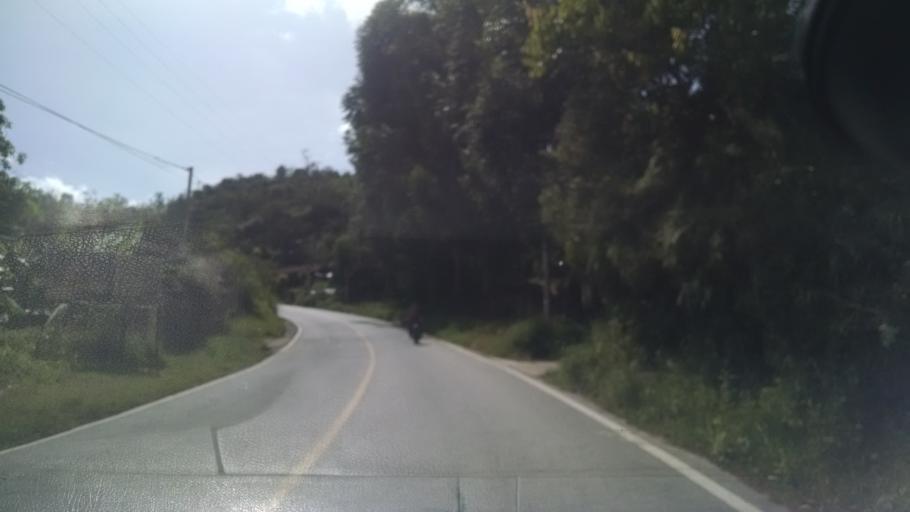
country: CO
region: Antioquia
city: San Vicente
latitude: 6.2236
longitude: -75.2521
